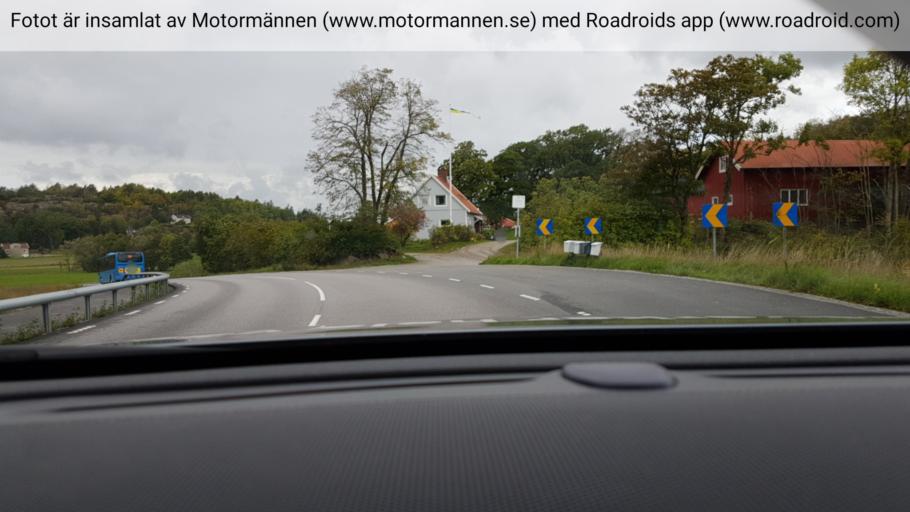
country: SE
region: Vaestra Goetaland
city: Svanesund
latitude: 58.1269
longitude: 11.8573
